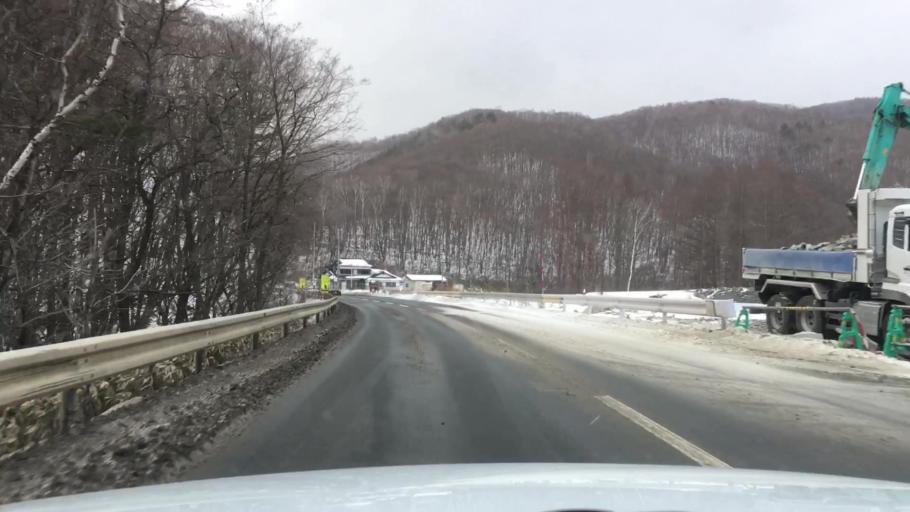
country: JP
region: Iwate
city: Morioka-shi
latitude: 39.6337
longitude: 141.4516
